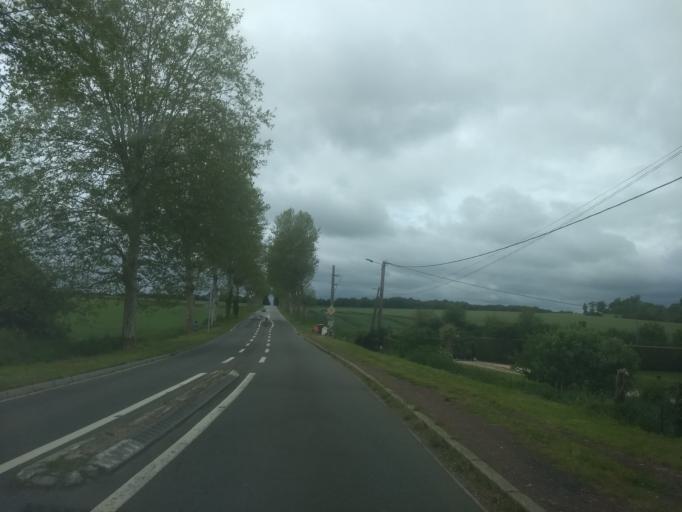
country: FR
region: Centre
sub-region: Departement d'Eure-et-Loir
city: Treon
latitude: 48.6744
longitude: 1.3226
